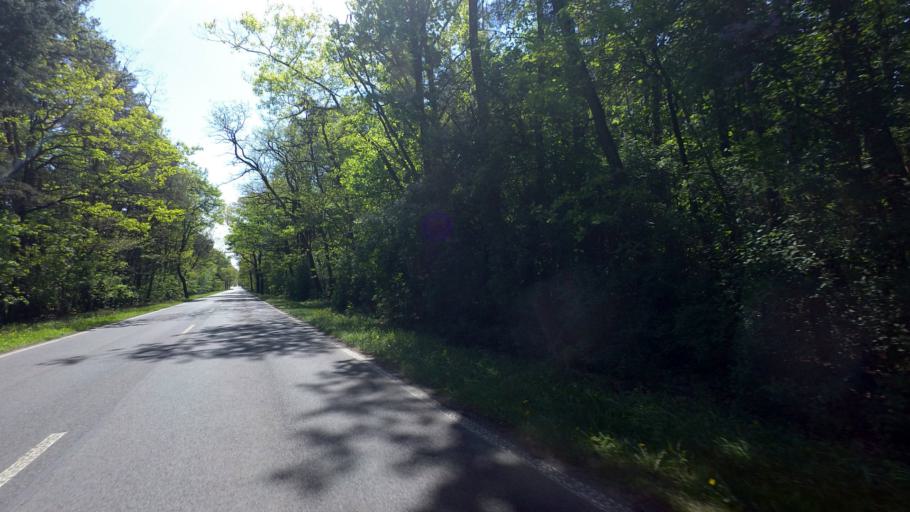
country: DE
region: Brandenburg
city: Bestensee
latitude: 52.2539
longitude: 13.6553
